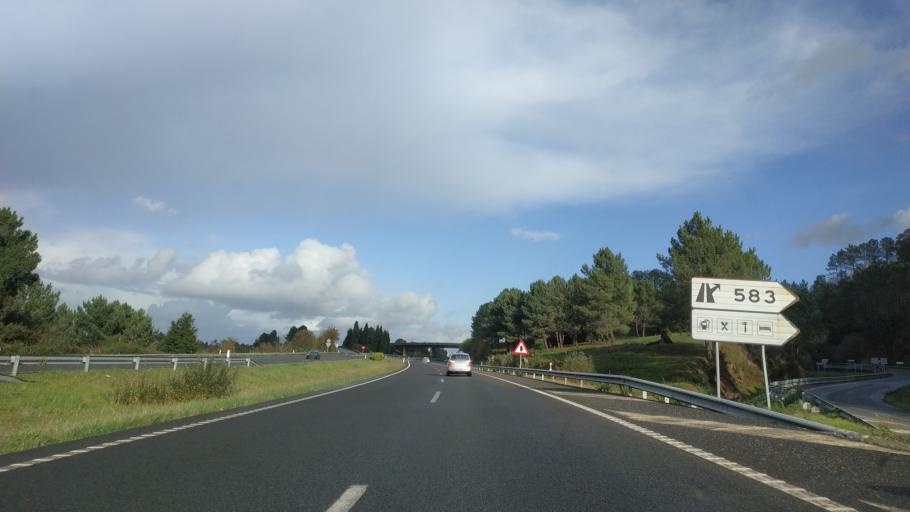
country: ES
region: Galicia
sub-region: Provincia da Coruna
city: Culleredo
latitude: 43.2723
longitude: -8.3732
